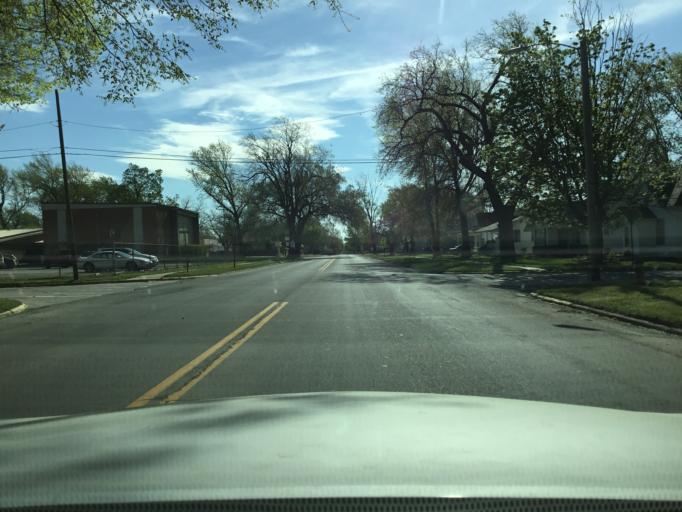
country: US
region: Kansas
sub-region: Neosho County
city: Chanute
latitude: 37.6820
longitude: -95.4678
